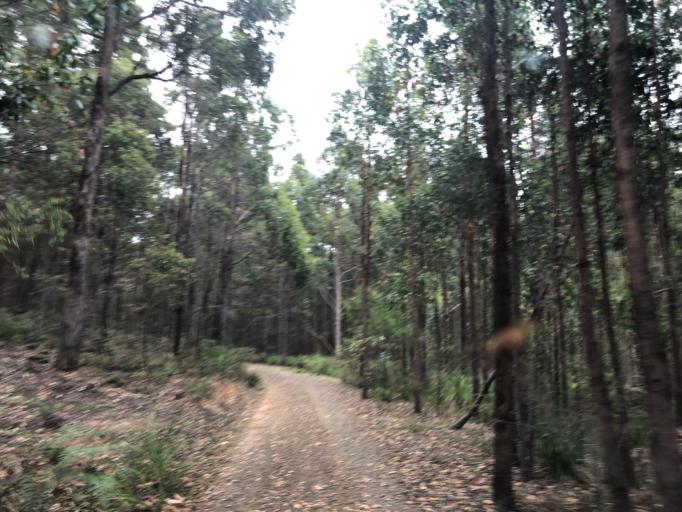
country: AU
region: Victoria
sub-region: Moorabool
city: Bacchus Marsh
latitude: -37.4410
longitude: 144.2468
